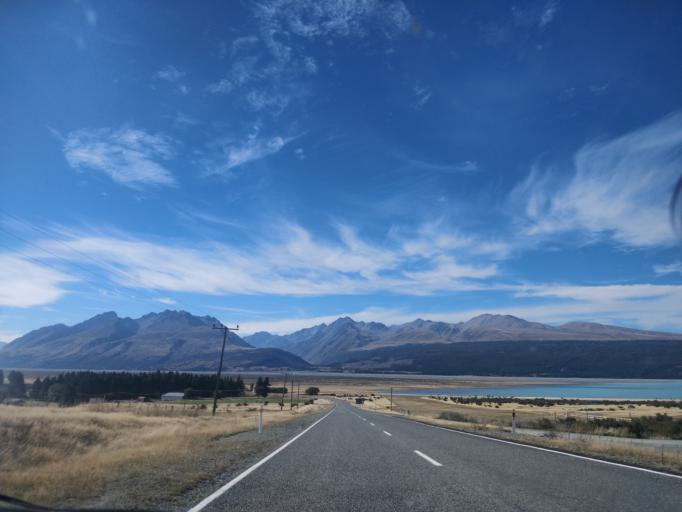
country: NZ
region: Canterbury
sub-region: Timaru District
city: Pleasant Point
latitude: -43.9118
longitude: 170.1205
